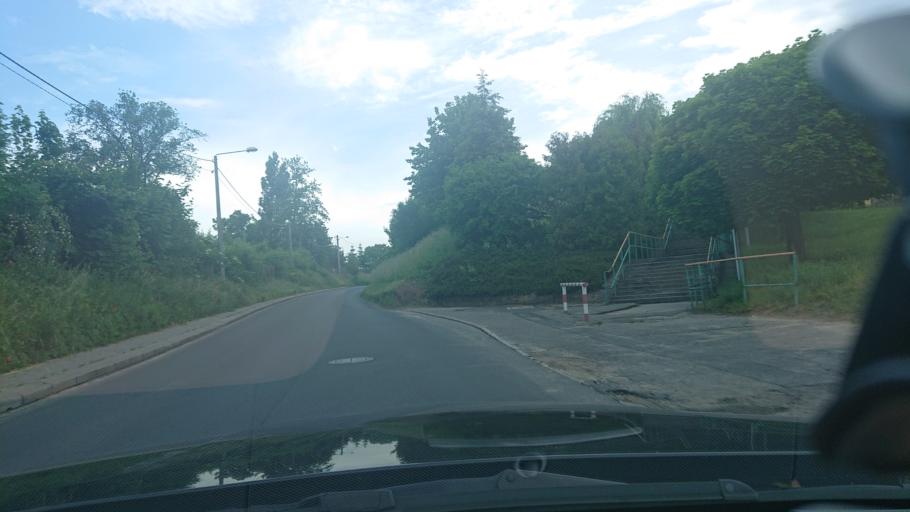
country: PL
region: Greater Poland Voivodeship
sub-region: Powiat gnieznienski
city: Gniezno
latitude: 52.5401
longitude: 17.5884
